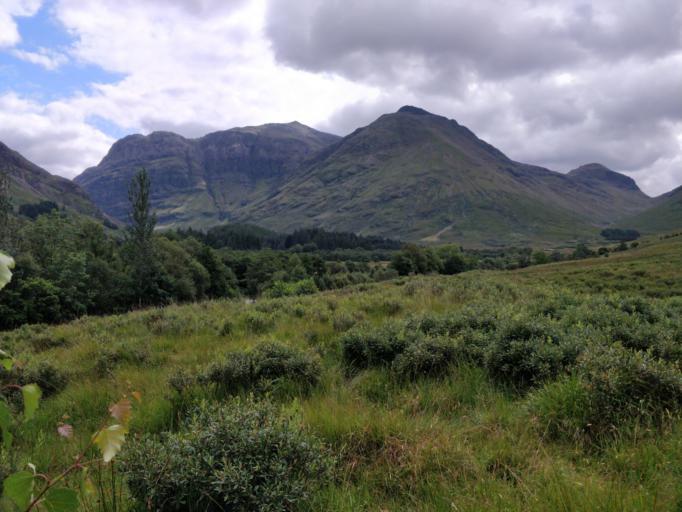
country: GB
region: Scotland
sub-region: Highland
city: Fort William
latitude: 56.6711
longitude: -5.0816
